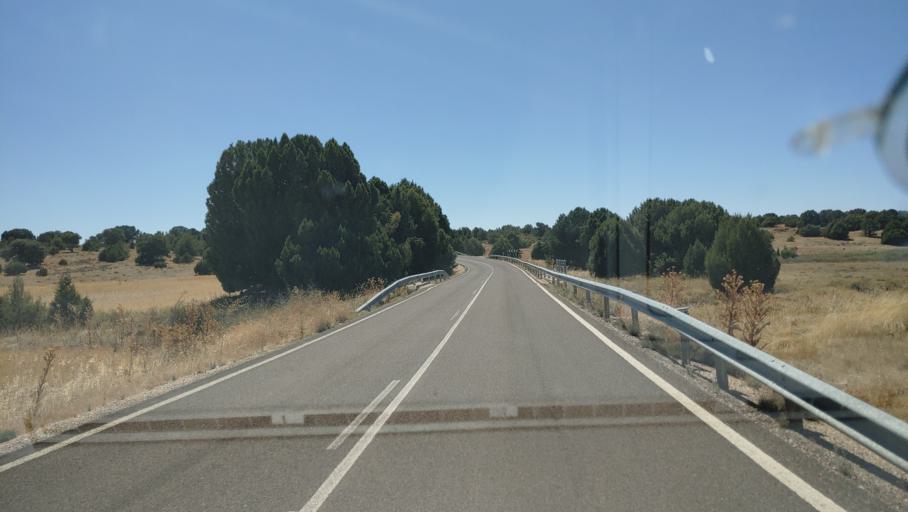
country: ES
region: Castille-La Mancha
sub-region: Provincia de Albacete
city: Ossa de Montiel
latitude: 38.8653
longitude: -2.7990
